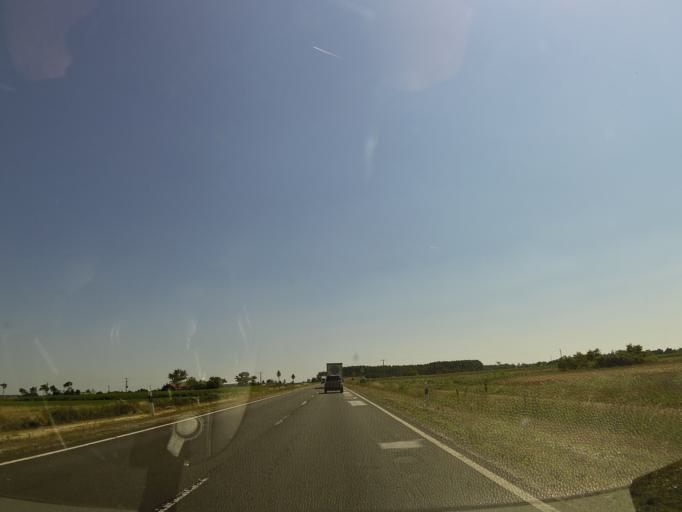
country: HU
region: Jasz-Nagykun-Szolnok
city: Torokszentmiklos
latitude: 47.1879
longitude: 20.3901
